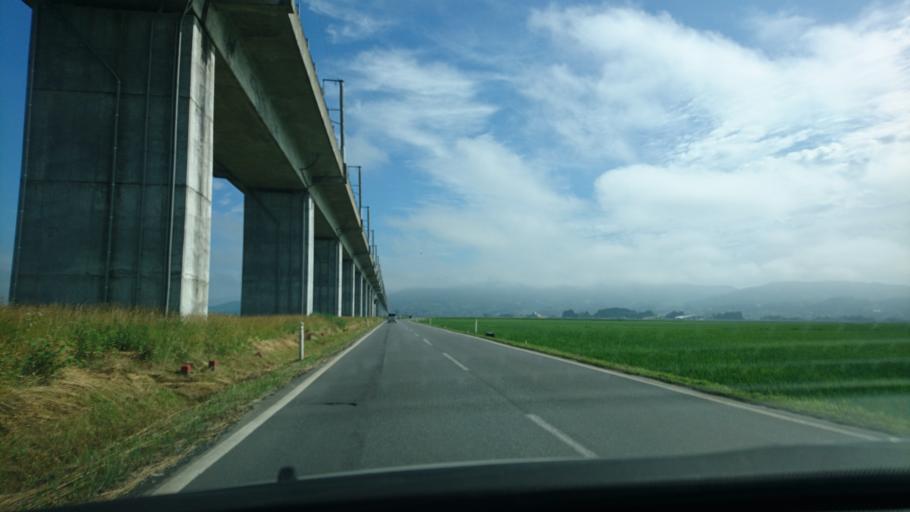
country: JP
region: Iwate
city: Ichinoseki
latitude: 38.9449
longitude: 141.1468
